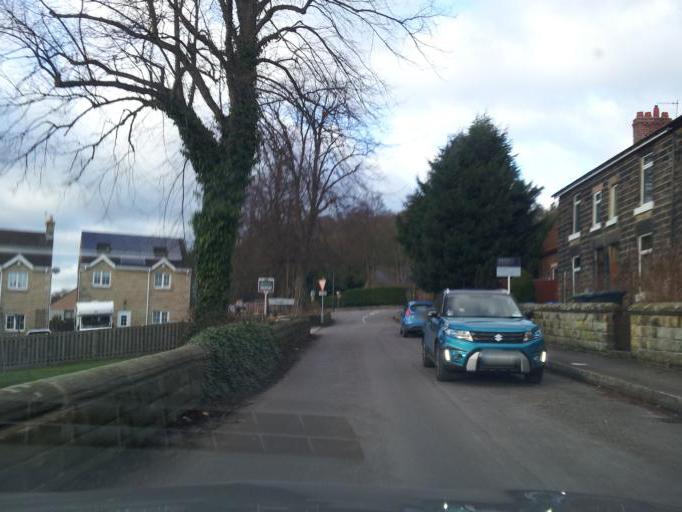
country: GB
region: England
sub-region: Derbyshire
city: Matlock
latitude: 53.1675
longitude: -1.6021
